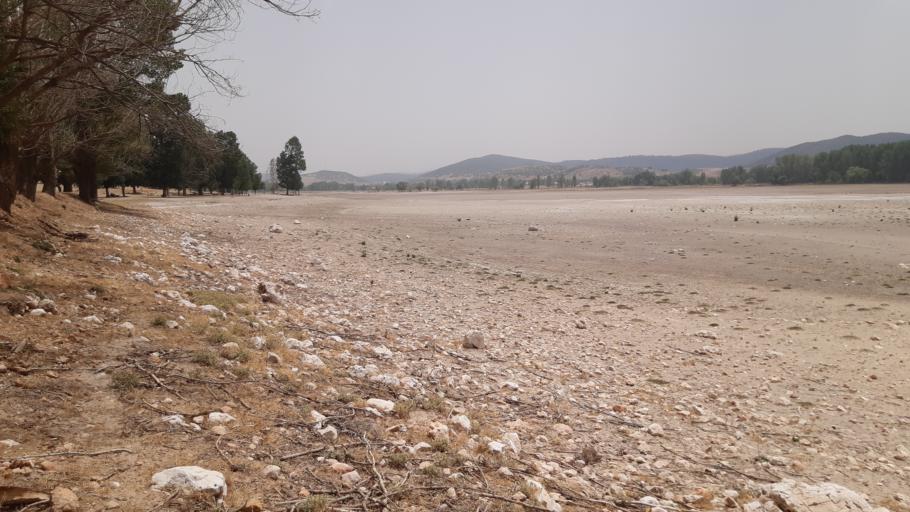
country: MA
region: Meknes-Tafilalet
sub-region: Ifrane
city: Ifrane
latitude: 33.6550
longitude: -5.0371
